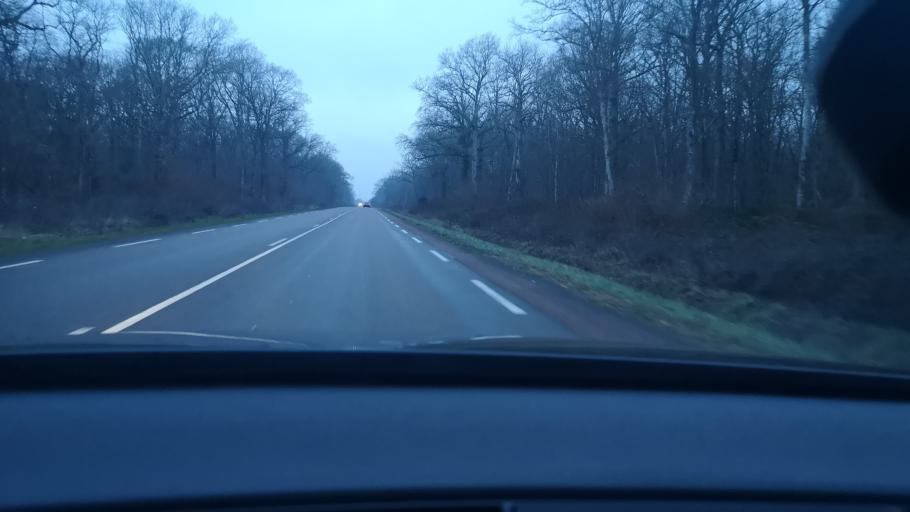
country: FR
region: Bourgogne
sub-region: Departement de Saone-et-Loire
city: Verdun-sur-le-Doubs
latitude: 47.0052
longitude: 5.0355
